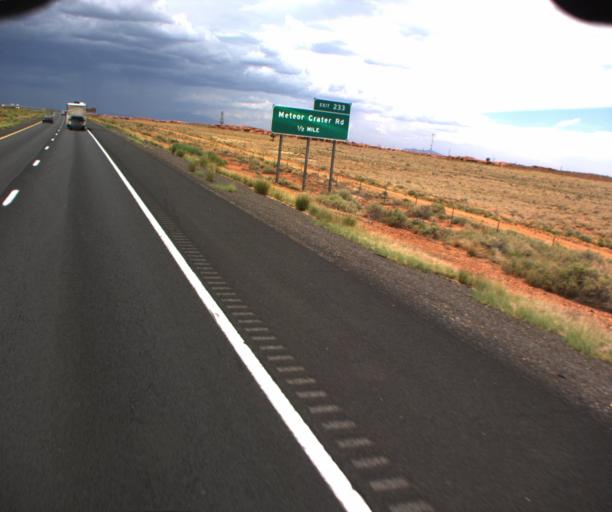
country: US
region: Arizona
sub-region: Coconino County
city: LeChee
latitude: 35.1083
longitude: -111.0167
